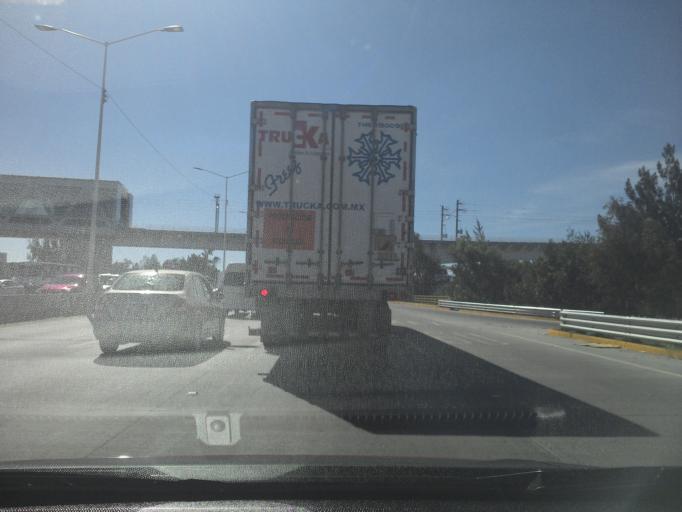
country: MX
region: Jalisco
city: Zapopan2
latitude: 20.7396
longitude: -103.4028
